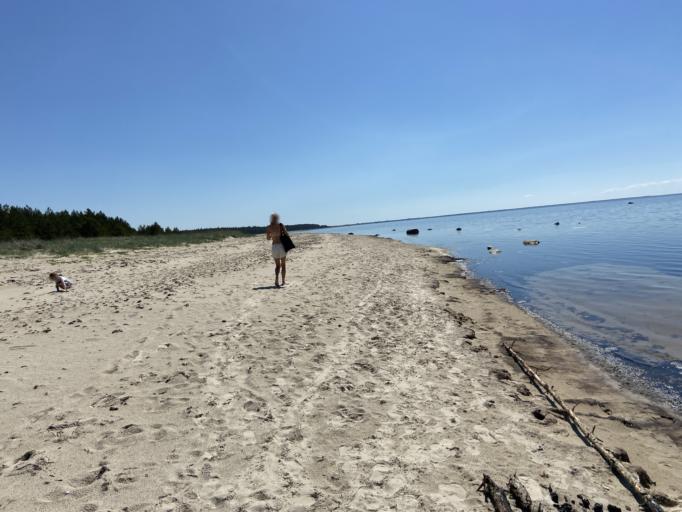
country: EE
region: Laeaene
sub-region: Haapsalu linn
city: Haapsalu
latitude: 59.1606
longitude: 23.5122
